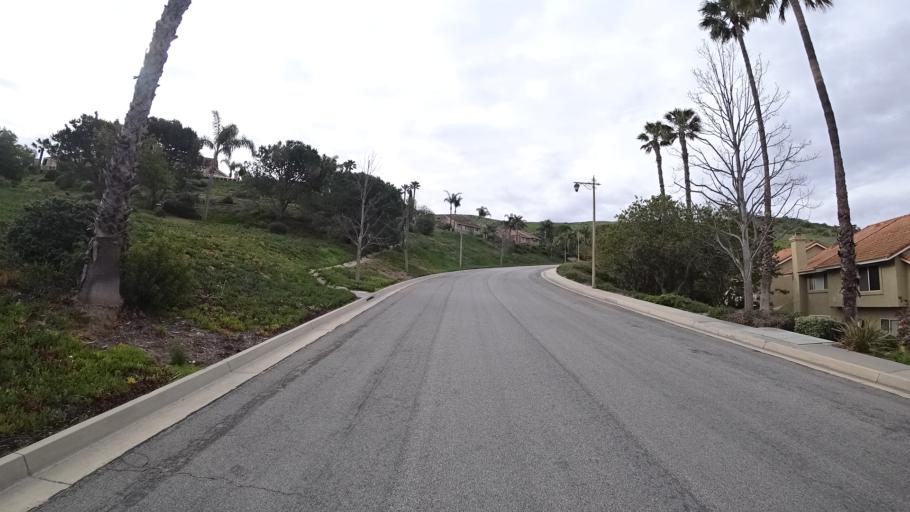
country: US
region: California
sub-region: Orange County
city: Villa Park
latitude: 33.8356
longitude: -117.7820
